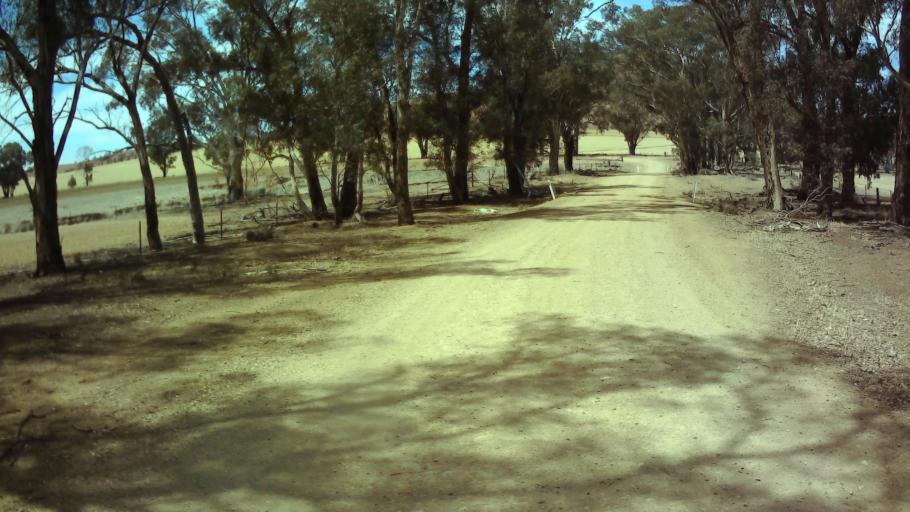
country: AU
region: New South Wales
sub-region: Weddin
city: Grenfell
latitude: -33.7582
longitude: 148.1409
